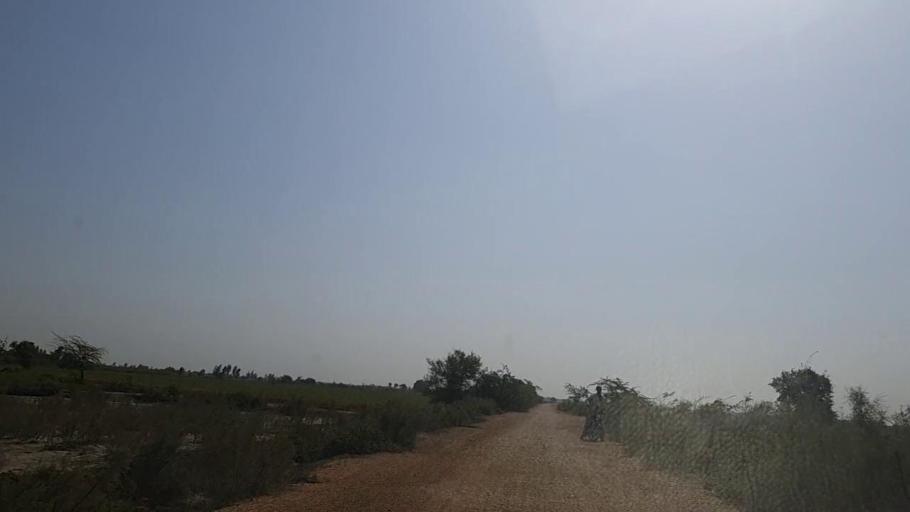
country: PK
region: Sindh
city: Daro Mehar
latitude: 24.7118
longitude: 68.1222
